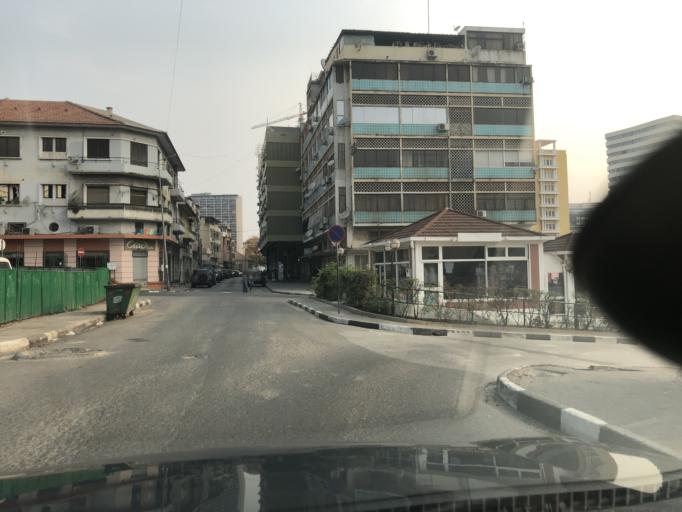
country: AO
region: Luanda
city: Luanda
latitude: -8.8166
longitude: 13.2331
